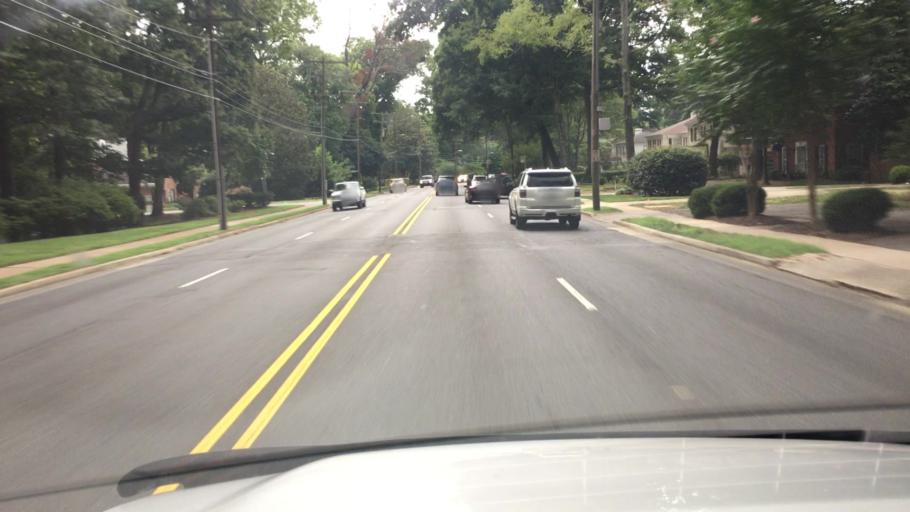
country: US
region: North Carolina
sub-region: Mecklenburg County
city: Charlotte
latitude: 35.1927
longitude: -80.8246
